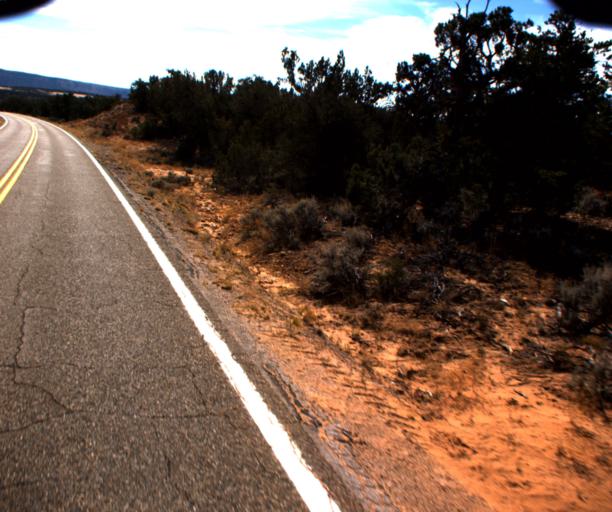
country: US
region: Arizona
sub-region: Navajo County
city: Kayenta
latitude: 36.6210
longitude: -110.5079
